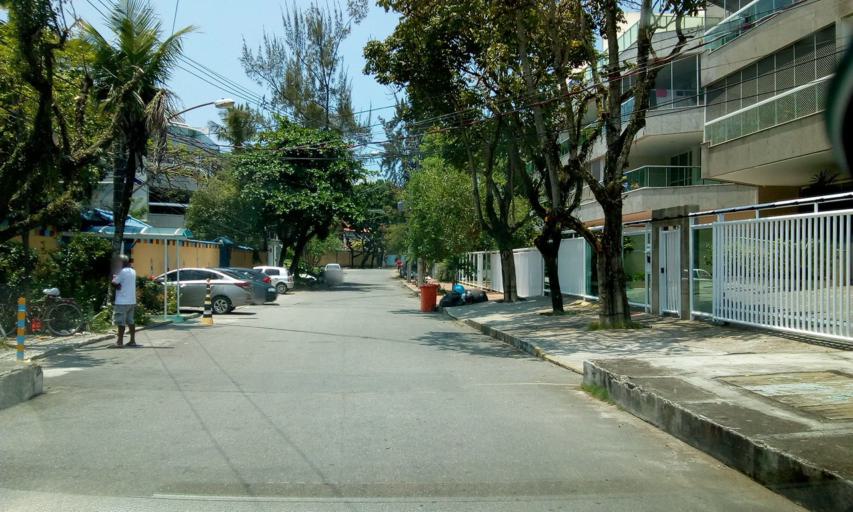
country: BR
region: Rio de Janeiro
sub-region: Nilopolis
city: Nilopolis
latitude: -23.0210
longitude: -43.4698
